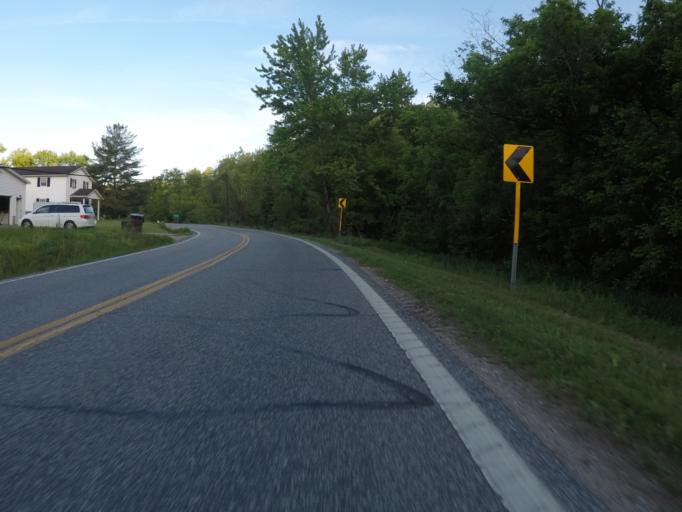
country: US
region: West Virginia
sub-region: Cabell County
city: Huntington
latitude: 38.4903
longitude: -82.4770
